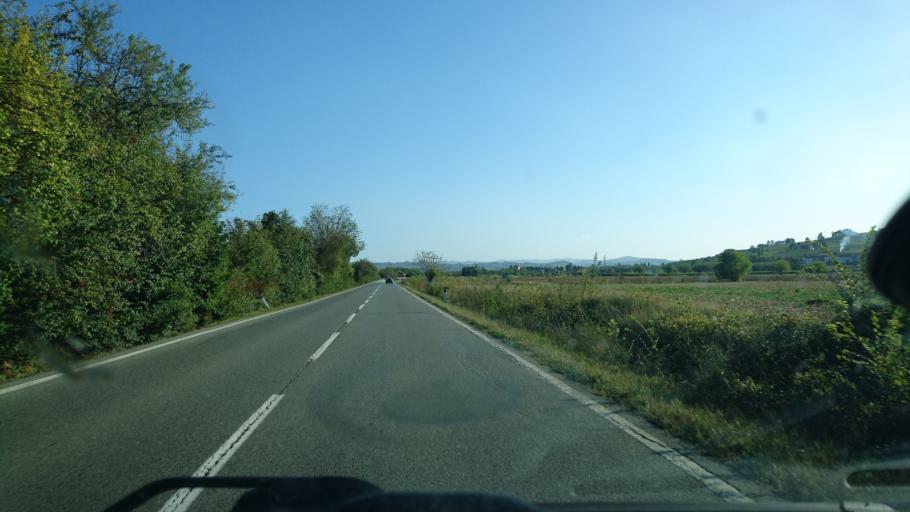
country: IT
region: Piedmont
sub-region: Provincia di Alessandria
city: Strevi
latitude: 44.7225
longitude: 8.5284
